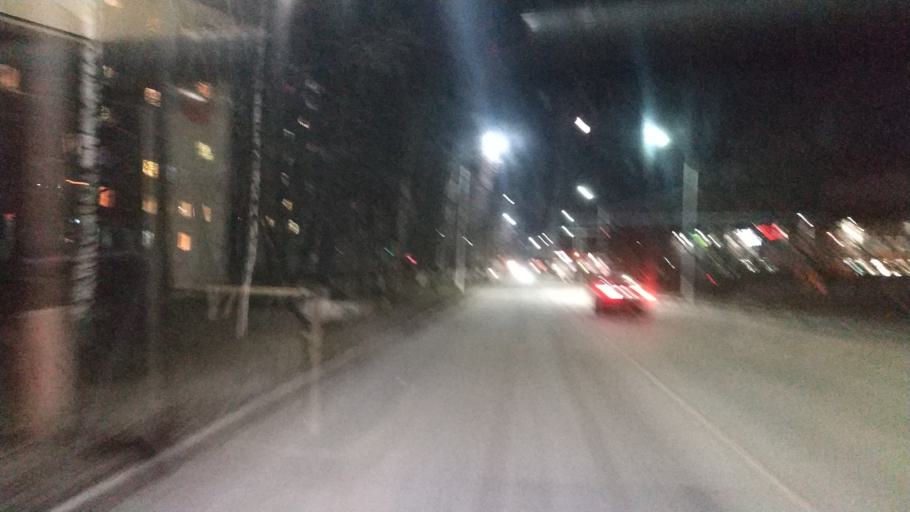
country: RU
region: Moskovskaya
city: Dubrovitsy
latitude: 55.4332
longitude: 37.4952
